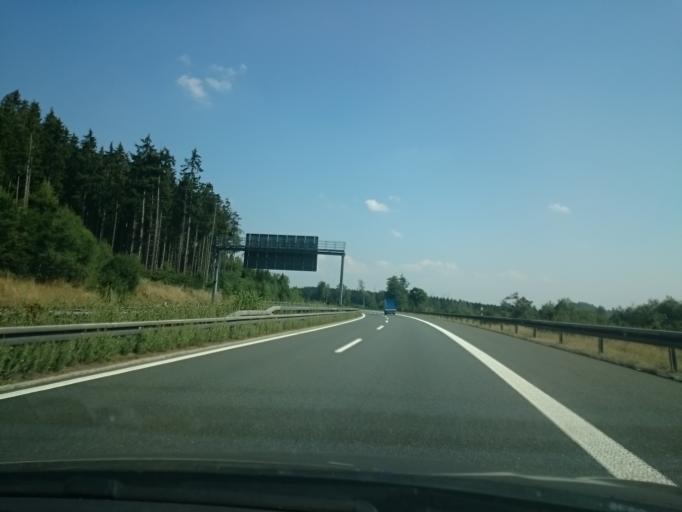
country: DE
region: Bavaria
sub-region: Upper Franconia
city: Leupoldsgrun
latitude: 50.3327
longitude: 11.8118
